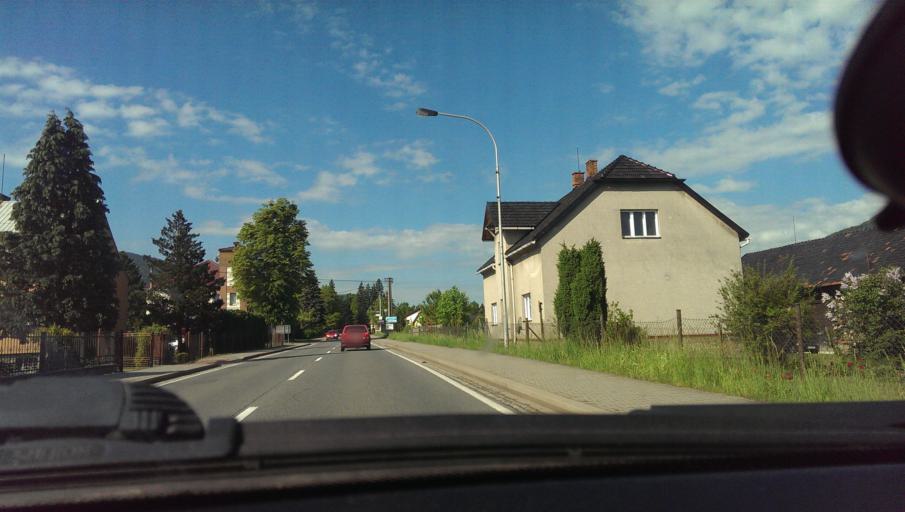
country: CZ
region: Moravskoslezsky
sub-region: Okres Frydek-Mistek
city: Celadna
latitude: 49.5464
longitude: 18.3355
